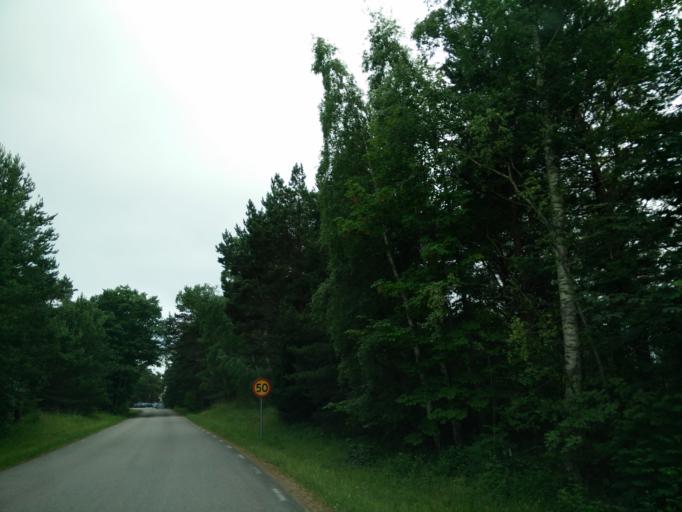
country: SE
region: Gotland
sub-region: Gotland
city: Slite
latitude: 57.9698
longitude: 19.2334
